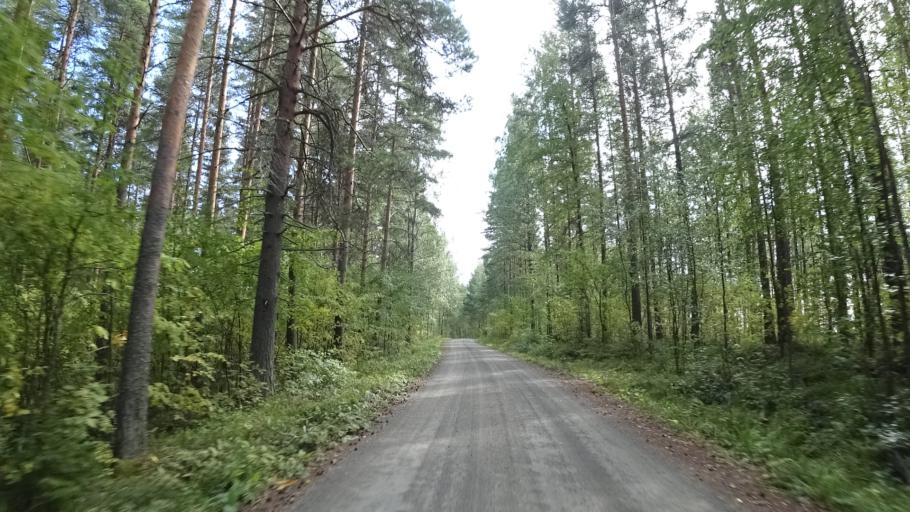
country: FI
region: North Karelia
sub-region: Keski-Karjala
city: Raeaekkylae
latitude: 62.3935
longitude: 29.7709
